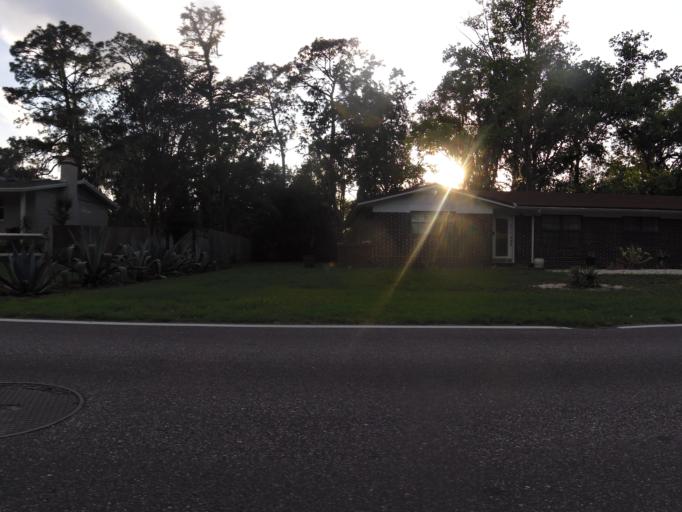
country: US
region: Florida
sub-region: Clay County
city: Orange Park
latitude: 30.2251
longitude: -81.6092
